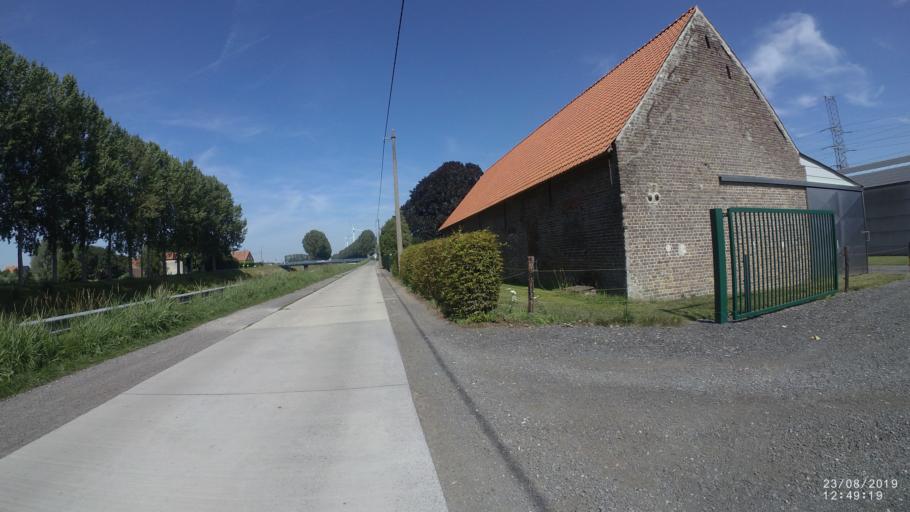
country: BE
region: Flanders
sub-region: Provincie Oost-Vlaanderen
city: Eeklo
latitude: 51.1689
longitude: 3.5413
